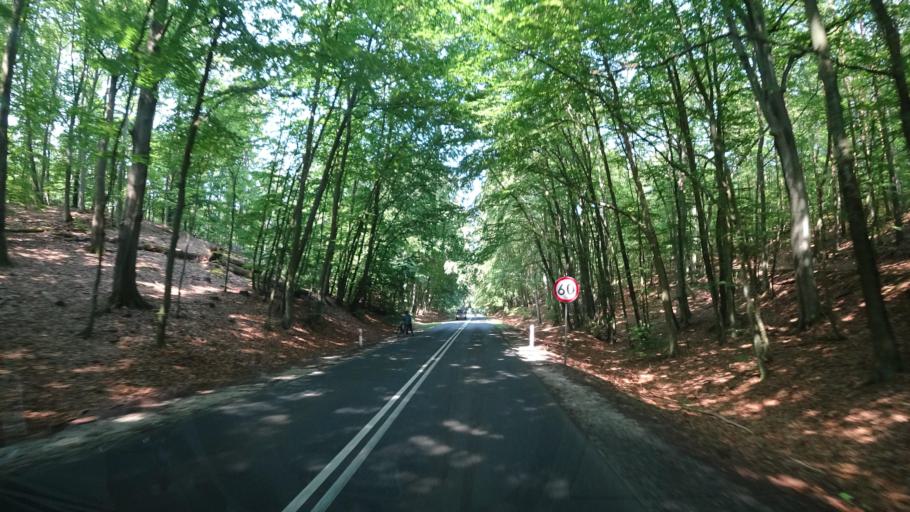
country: PL
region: West Pomeranian Voivodeship
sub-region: Powiat kamienski
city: Miedzyzdroje
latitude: 53.9496
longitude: 14.4903
